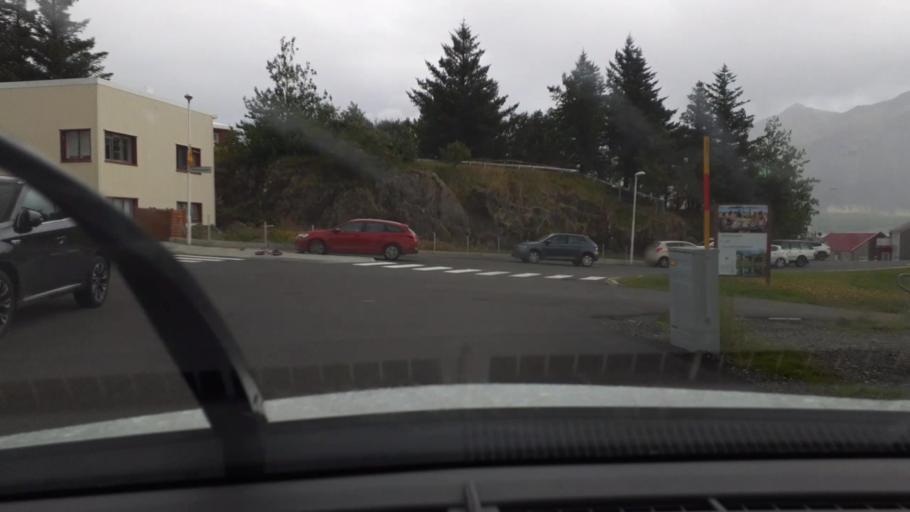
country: IS
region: West
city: Borgarnes
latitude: 64.5379
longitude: -21.9260
